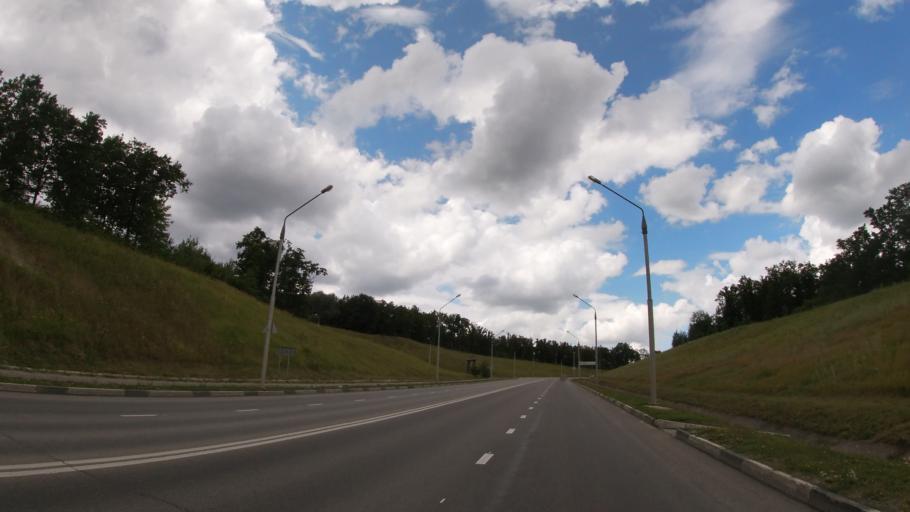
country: RU
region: Belgorod
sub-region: Belgorodskiy Rayon
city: Belgorod
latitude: 50.6219
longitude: 36.6140
